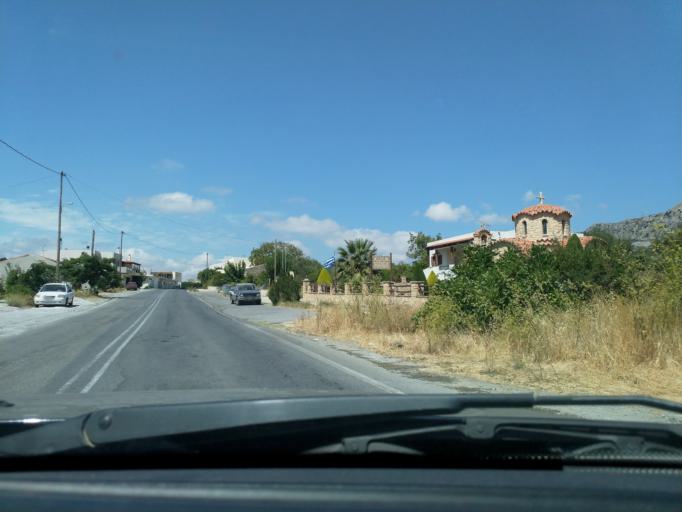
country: GR
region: Crete
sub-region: Nomos Rethymnis
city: Agia Foteini
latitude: 35.1857
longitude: 24.5560
